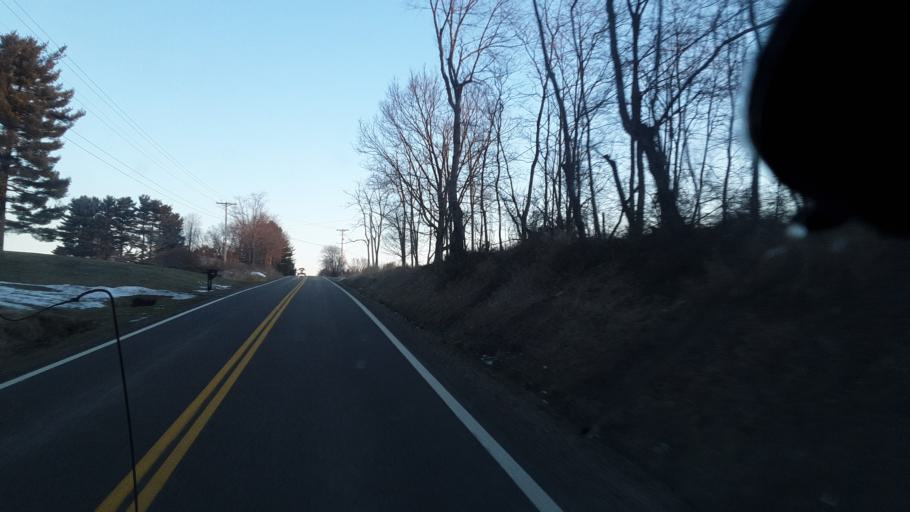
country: US
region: Ohio
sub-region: Perry County
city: Somerset
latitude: 39.7698
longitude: -82.3032
